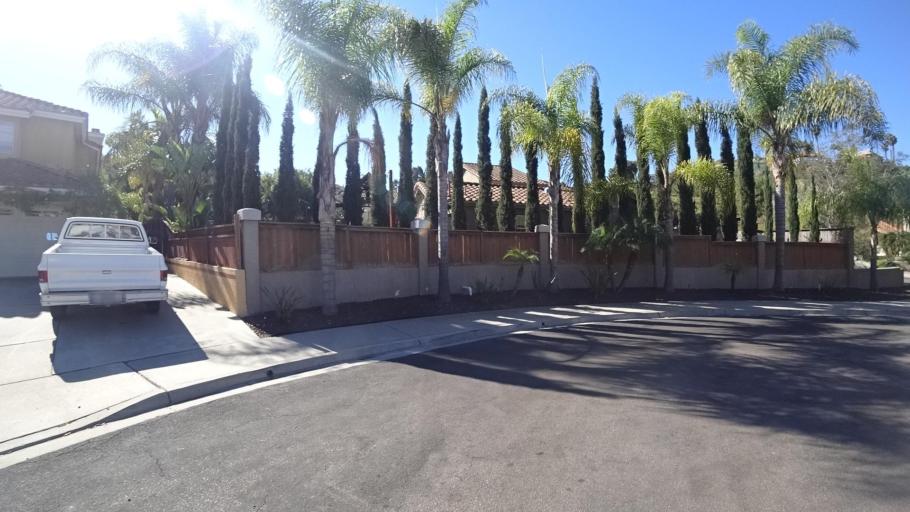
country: US
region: California
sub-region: San Diego County
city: Bonita
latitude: 32.6619
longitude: -117.0115
